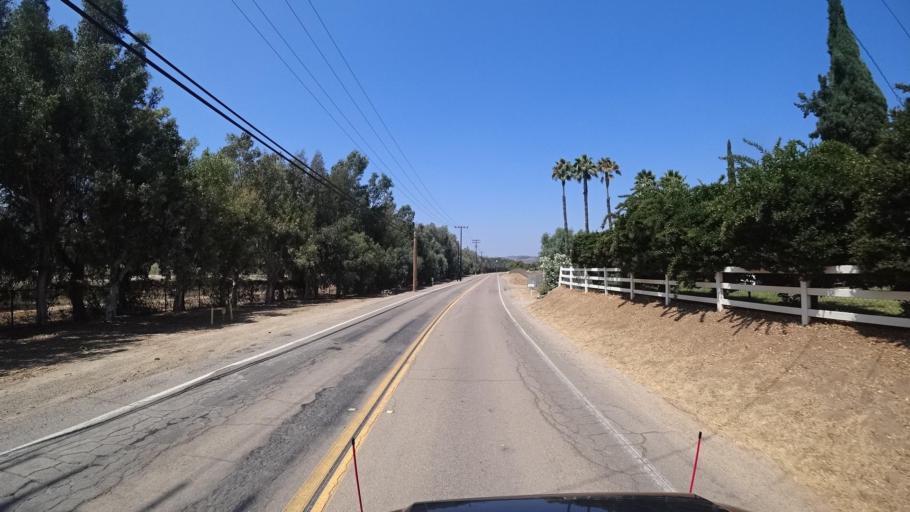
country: US
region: California
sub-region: San Diego County
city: Bonsall
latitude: 33.2831
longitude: -117.2017
